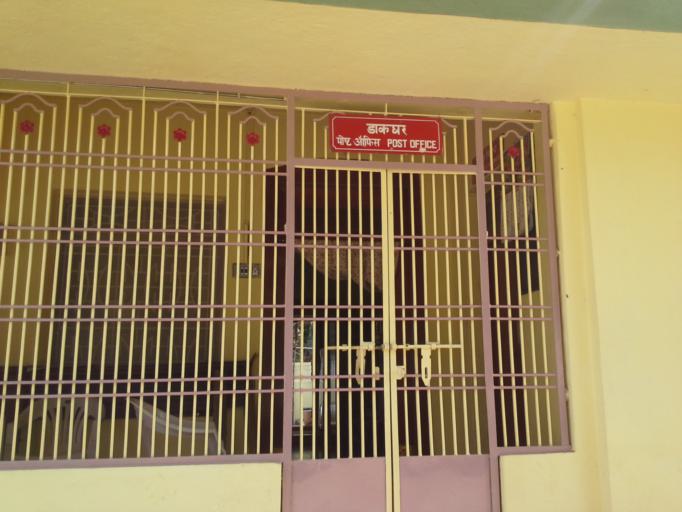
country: IN
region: Andhra Pradesh
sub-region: West Godavari
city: Kovvur
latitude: 17.0496
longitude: 81.7221
